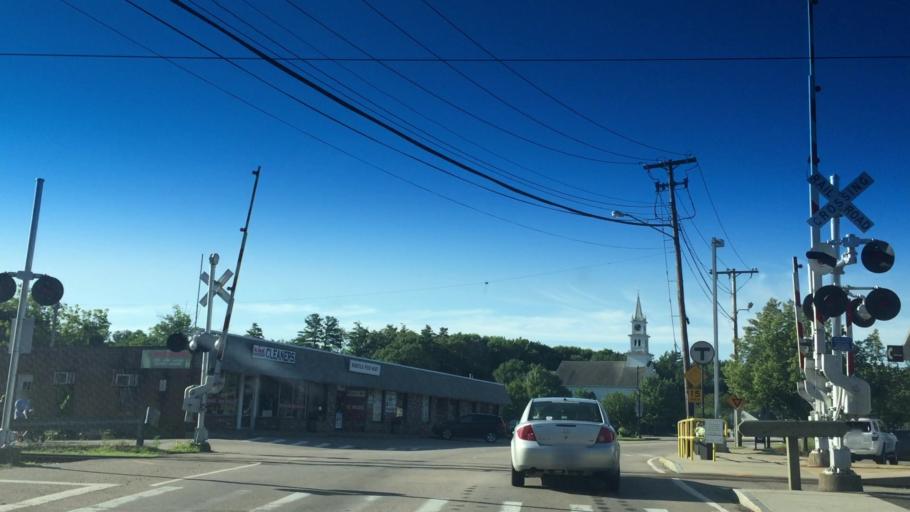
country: US
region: Massachusetts
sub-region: Norfolk County
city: Norfolk
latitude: 42.1207
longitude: -71.3255
